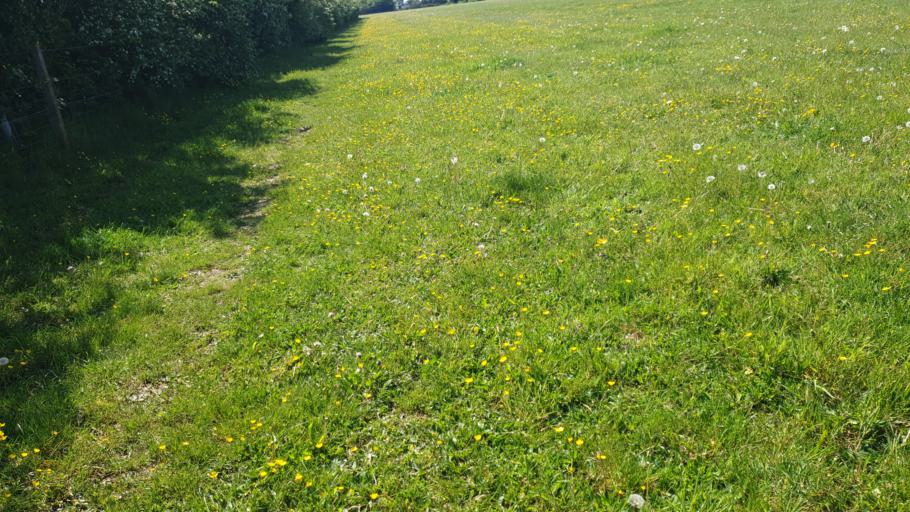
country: GB
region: England
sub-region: Essex
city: Manningtree
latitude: 51.9371
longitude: 1.0380
